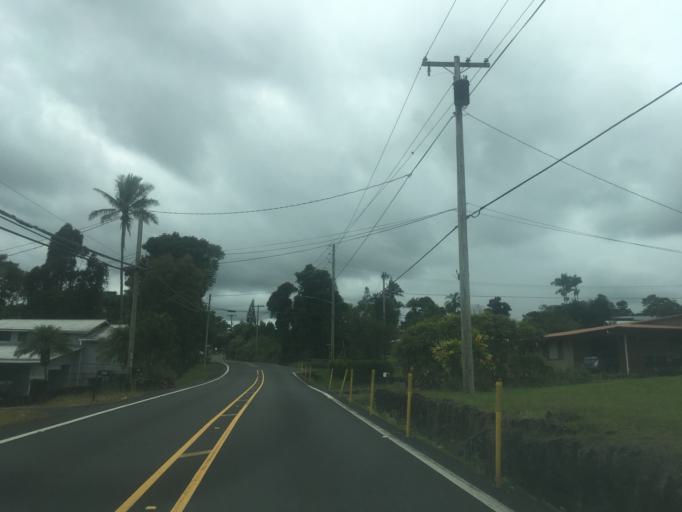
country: US
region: Hawaii
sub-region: Hawaii County
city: Hilo
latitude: 19.6963
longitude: -155.1179
